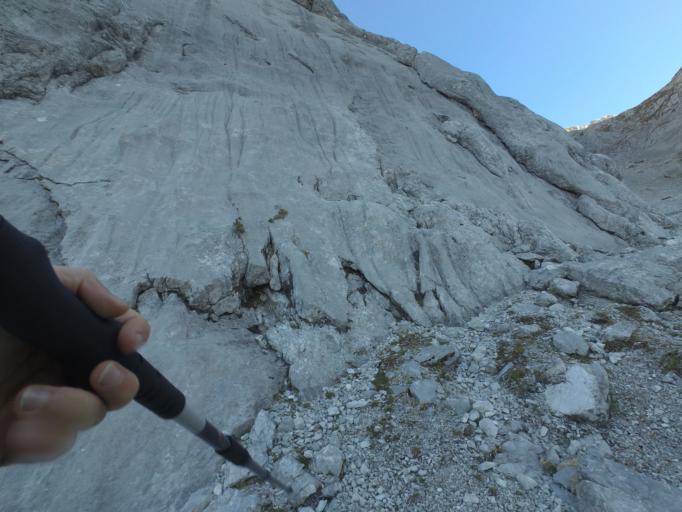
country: AT
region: Salzburg
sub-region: Politischer Bezirk Sankt Johann im Pongau
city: Werfenweng
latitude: 47.4953
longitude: 13.2334
